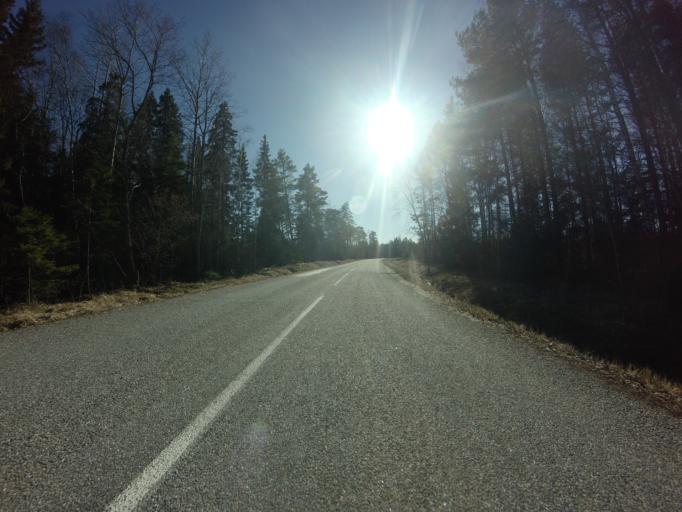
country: EE
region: Saare
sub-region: Kuressaare linn
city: Kuressaare
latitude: 58.5603
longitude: 22.3946
